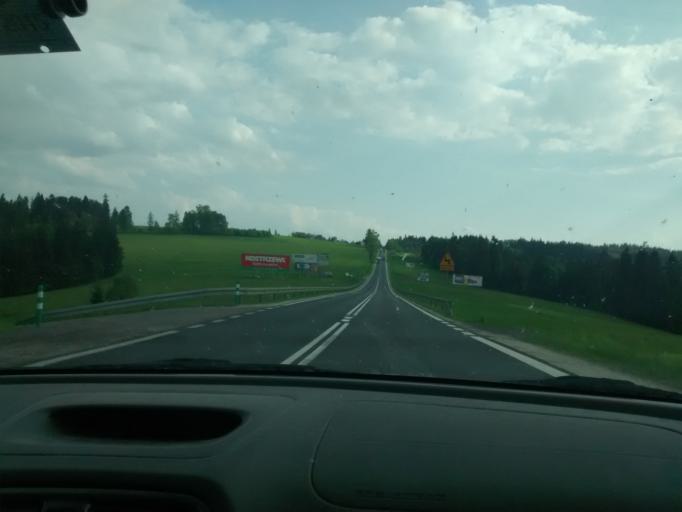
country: PL
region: Lesser Poland Voivodeship
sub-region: Powiat nowotarski
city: Rokiciny
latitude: 49.5686
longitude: 19.9458
